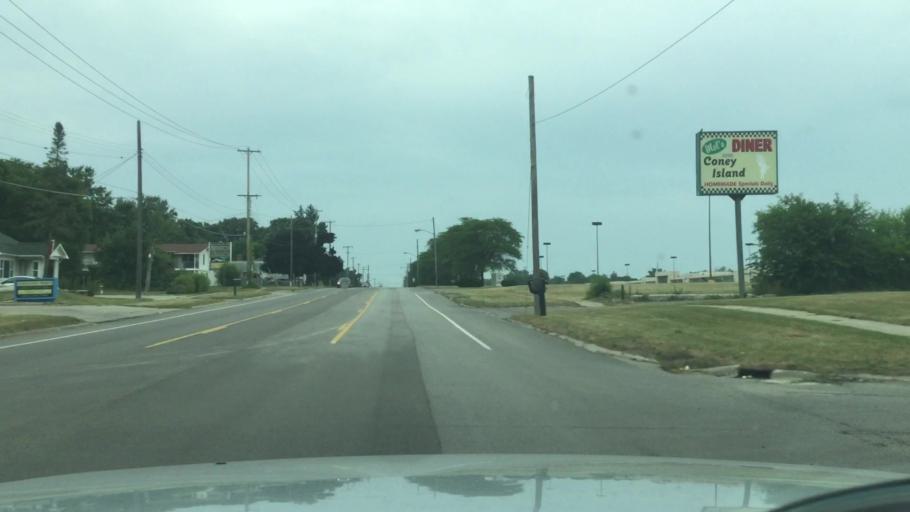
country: US
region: Michigan
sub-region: Genesee County
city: Flint
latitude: 42.9760
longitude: -83.6928
